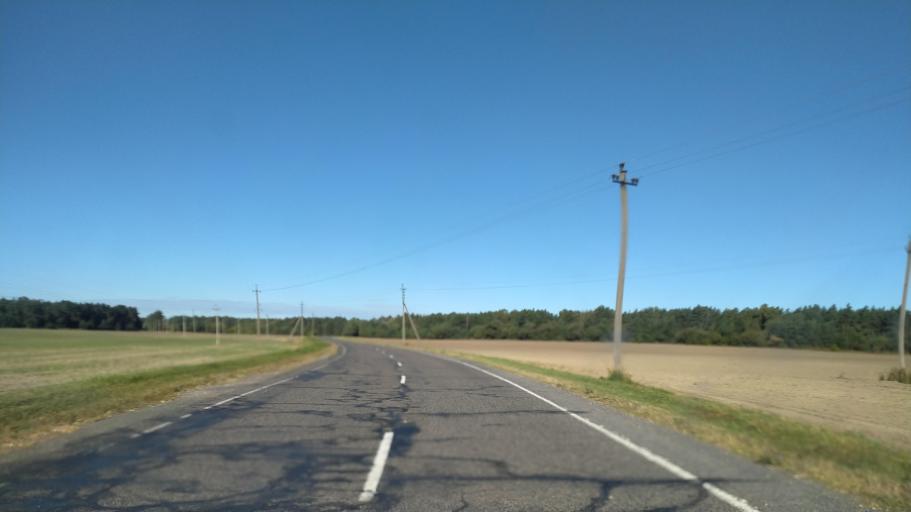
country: BY
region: Brest
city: Byaroza
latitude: 52.4890
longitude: 24.7385
